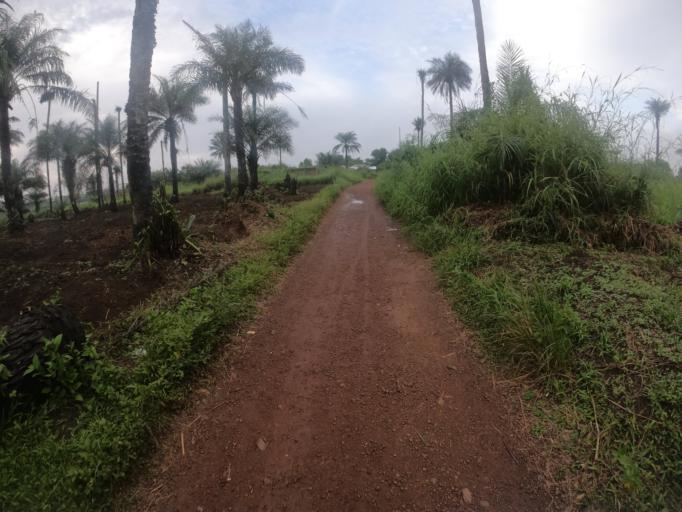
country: SL
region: Northern Province
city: Port Loko
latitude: 8.4978
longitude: -12.7511
